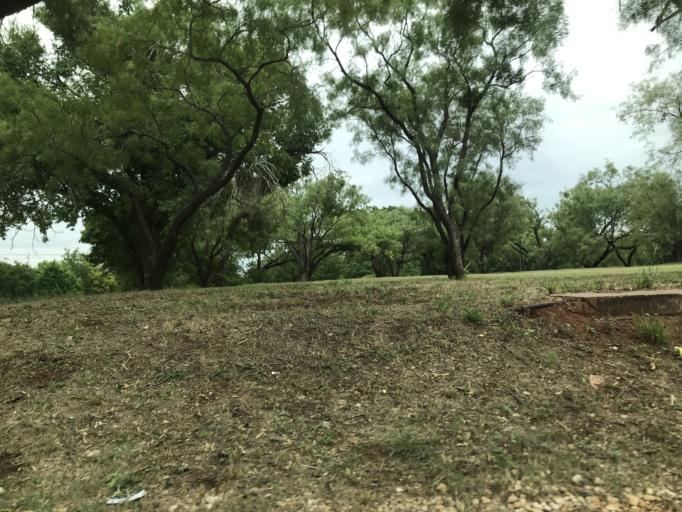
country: US
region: Texas
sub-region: Taylor County
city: Abilene
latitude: 32.4415
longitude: -99.7245
